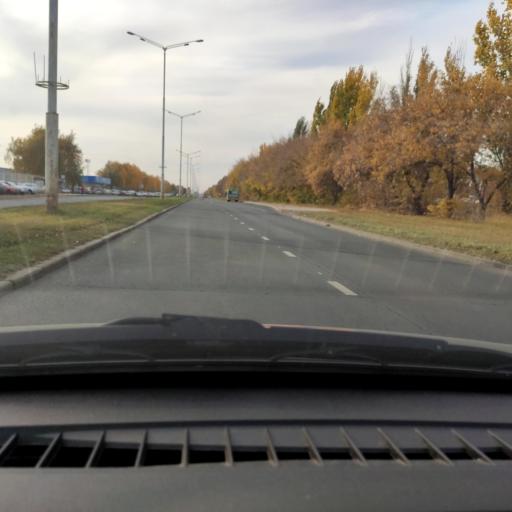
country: RU
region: Samara
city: Tol'yatti
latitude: 53.5705
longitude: 49.2469
